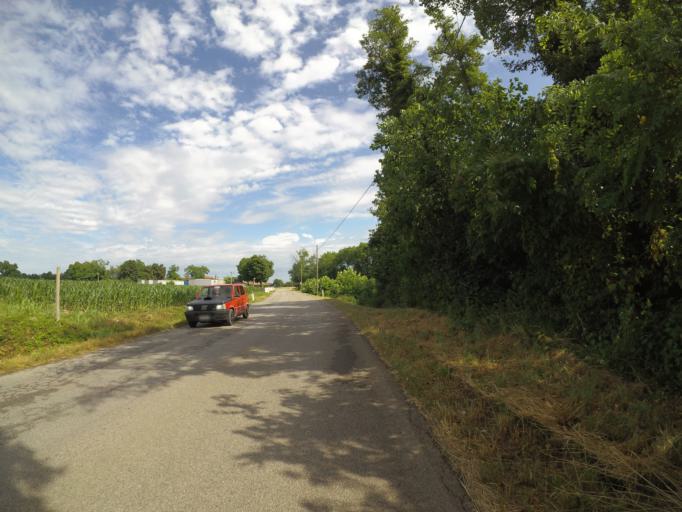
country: IT
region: Friuli Venezia Giulia
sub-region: Provincia di Udine
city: Lestizza
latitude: 45.9589
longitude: 13.1307
